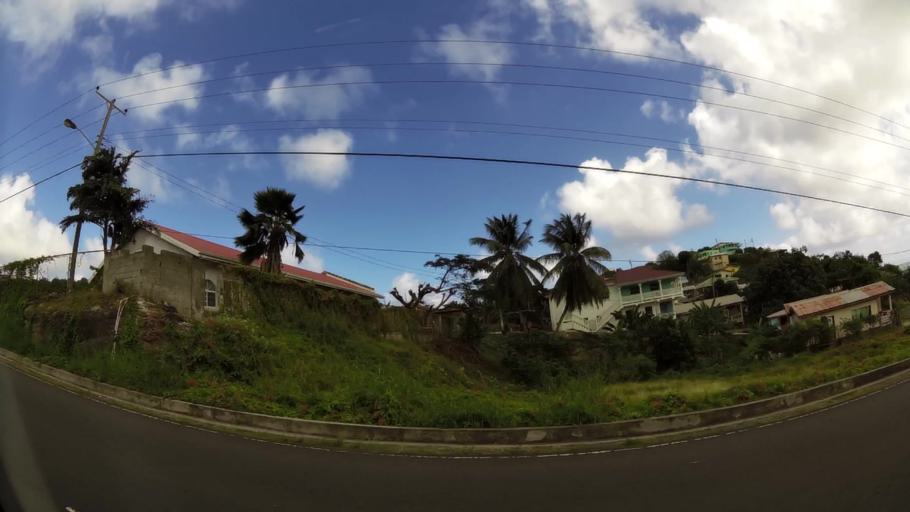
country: LC
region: Dennery Quarter
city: Dennery
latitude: 13.9128
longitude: -60.8948
